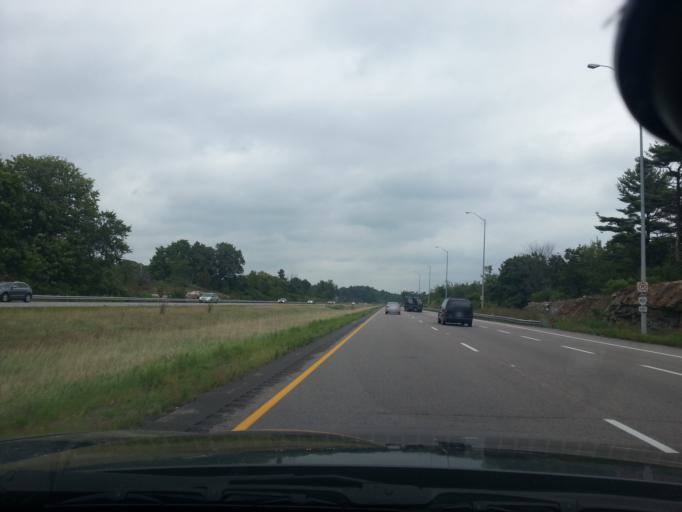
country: CA
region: Ontario
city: Brockville
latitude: 44.5091
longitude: -75.8338
